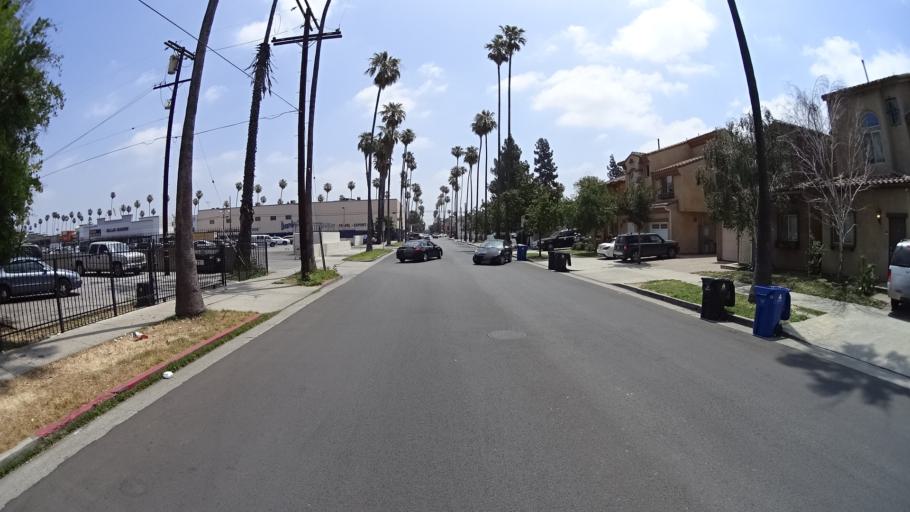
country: US
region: California
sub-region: Los Angeles County
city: Van Nuys
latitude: 34.1908
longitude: -118.4506
